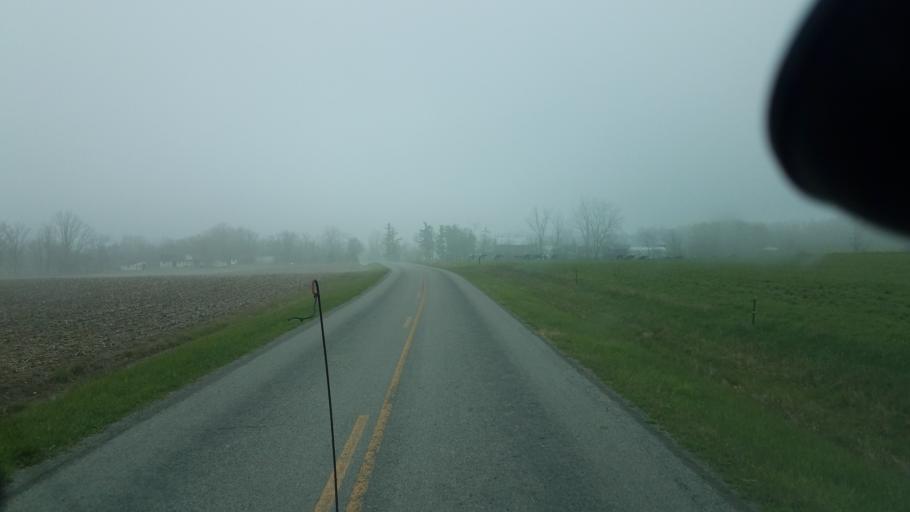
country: US
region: Ohio
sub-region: Logan County
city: Northwood
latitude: 40.4599
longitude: -83.7501
